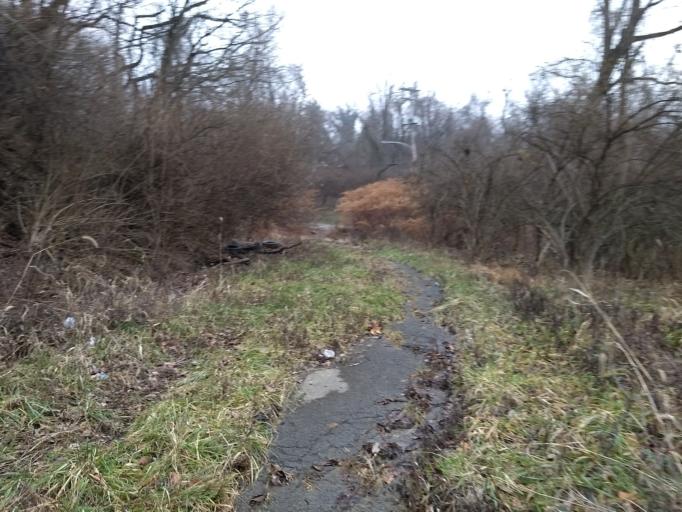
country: US
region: Pennsylvania
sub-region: Allegheny County
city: East Pittsburgh
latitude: 40.3862
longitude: -79.8454
